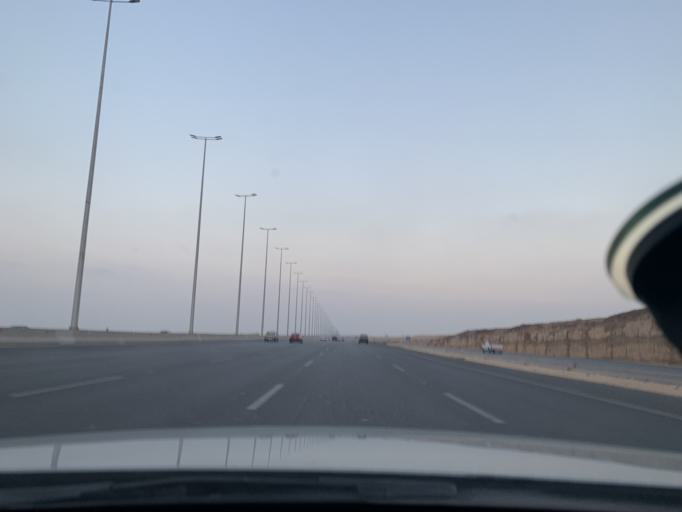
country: EG
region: Muhafazat al Qalyubiyah
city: Al Khankah
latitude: 30.0938
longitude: 31.4919
